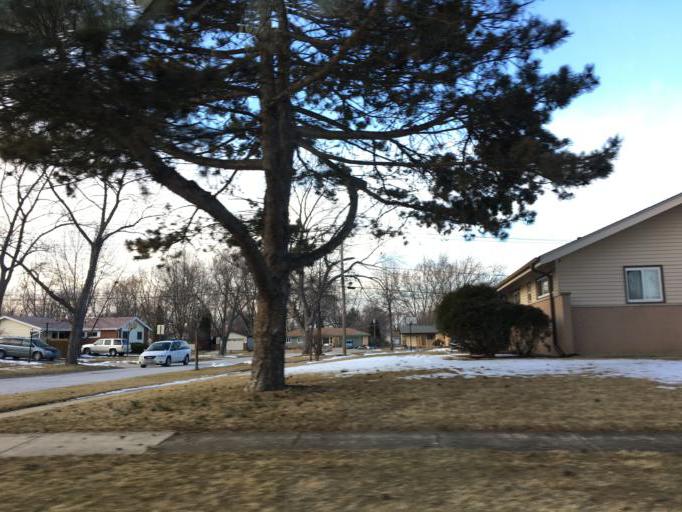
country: US
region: Illinois
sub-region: Cook County
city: Schaumburg
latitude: 42.0337
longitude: -88.0937
